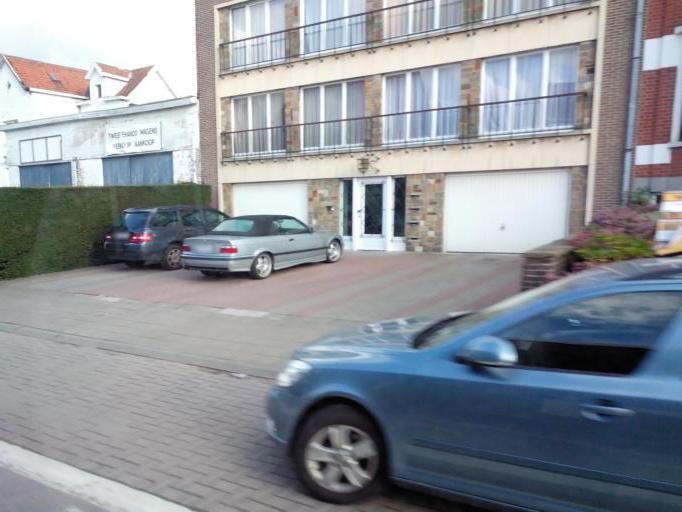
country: BE
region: Flanders
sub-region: Provincie Vlaams-Brabant
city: Kraainem
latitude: 50.8652
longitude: 4.4395
